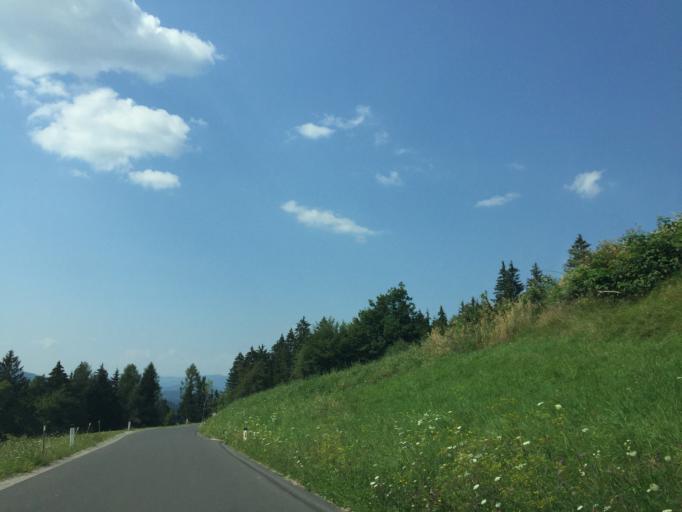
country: SI
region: Slovenj Gradec
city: Smartno pri Slovenj Gradcu
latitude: 46.4384
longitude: 15.1150
